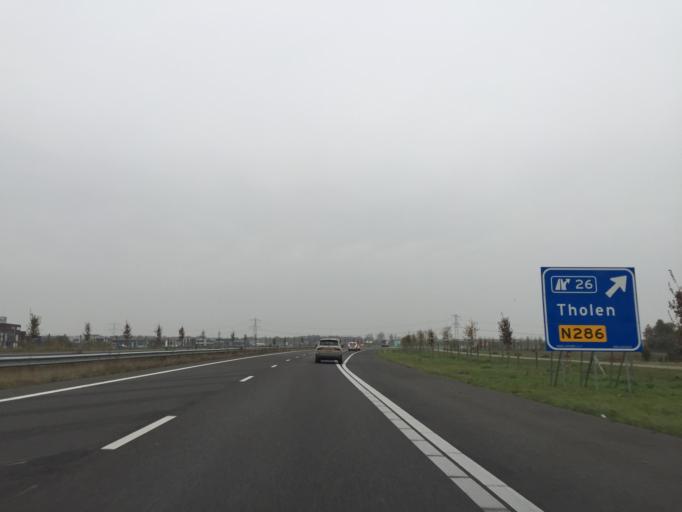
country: NL
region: North Brabant
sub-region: Gemeente Bergen op Zoom
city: Lepelstraat
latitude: 51.5361
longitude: 4.2975
